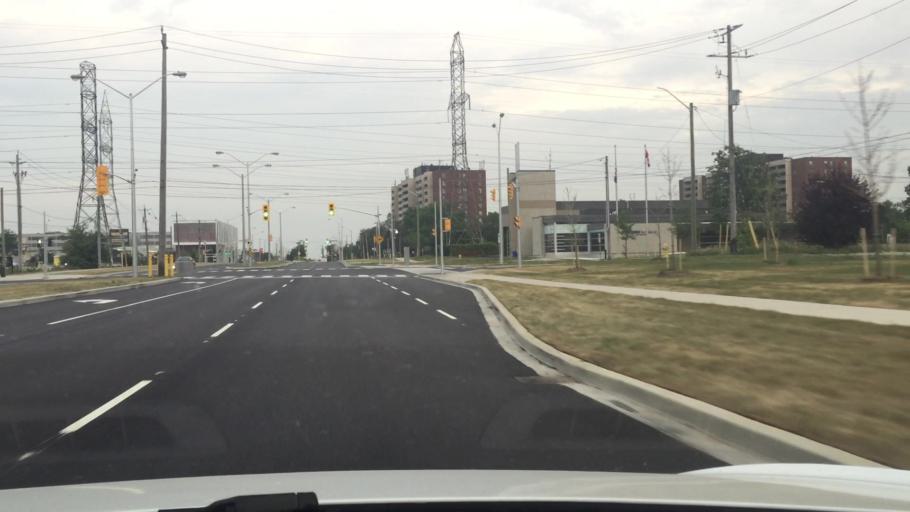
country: CA
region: Ontario
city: Concord
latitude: 43.7679
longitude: -79.4923
